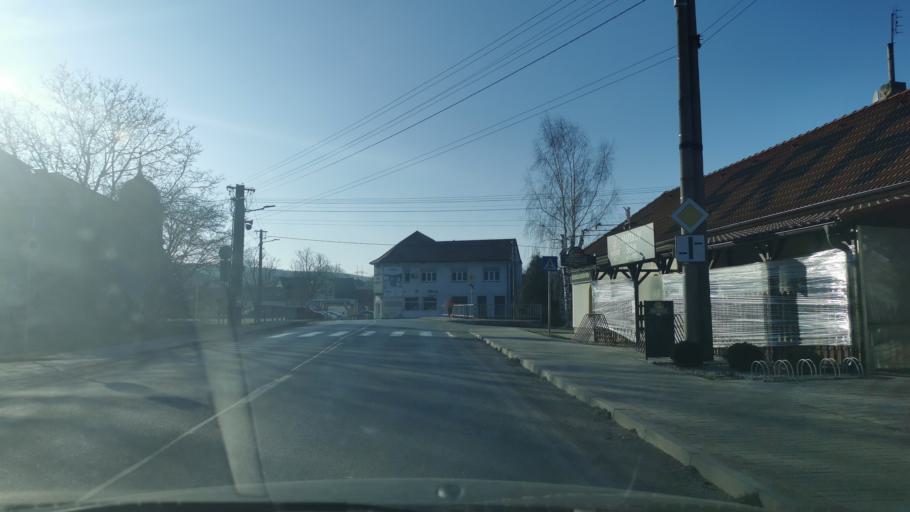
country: SK
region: Trnavsky
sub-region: Okres Senica
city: Senica
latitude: 48.7317
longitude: 17.4070
